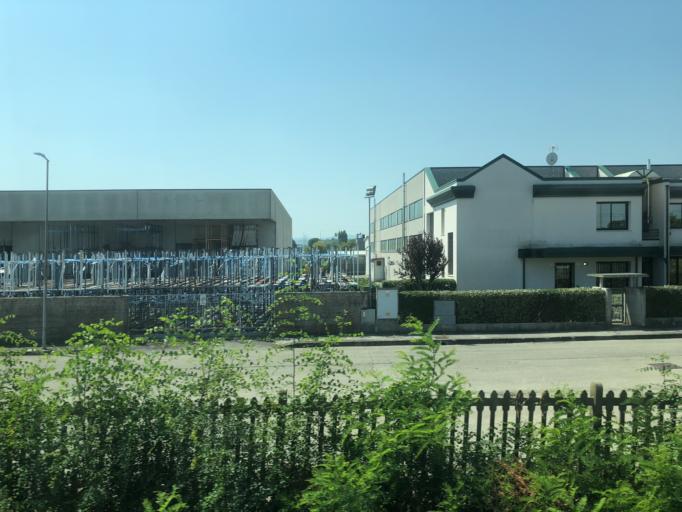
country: IT
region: Emilia-Romagna
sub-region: Provincia di Rimini
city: Santa Giustina
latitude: 44.0704
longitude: 12.4708
